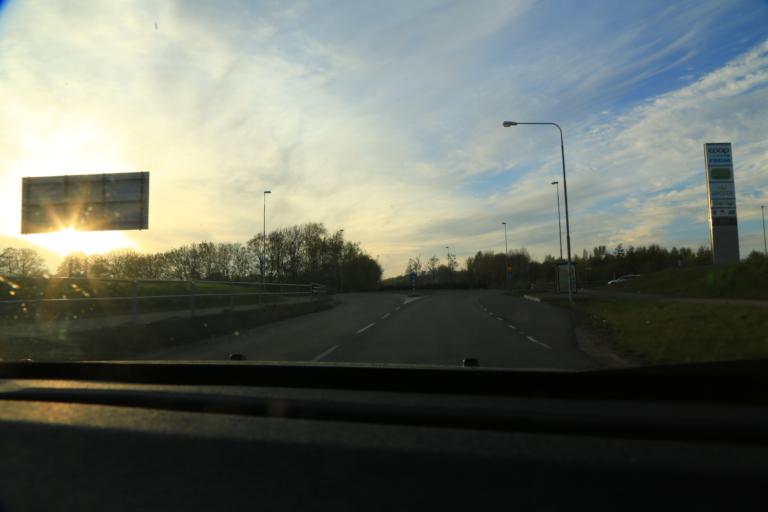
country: SE
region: Halland
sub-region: Varbergs Kommun
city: Traslovslage
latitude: 57.0823
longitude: 12.2762
